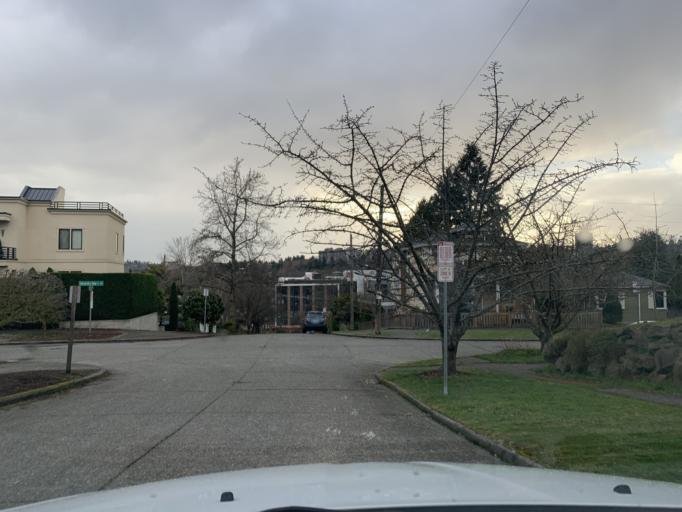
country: US
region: Washington
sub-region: King County
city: Seattle
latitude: 47.6638
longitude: -122.2926
